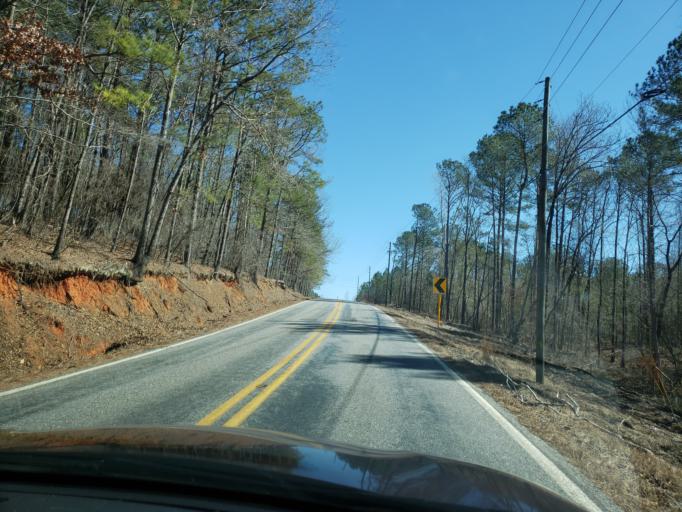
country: US
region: Alabama
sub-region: Elmore County
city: Tallassee
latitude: 32.6735
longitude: -85.8958
